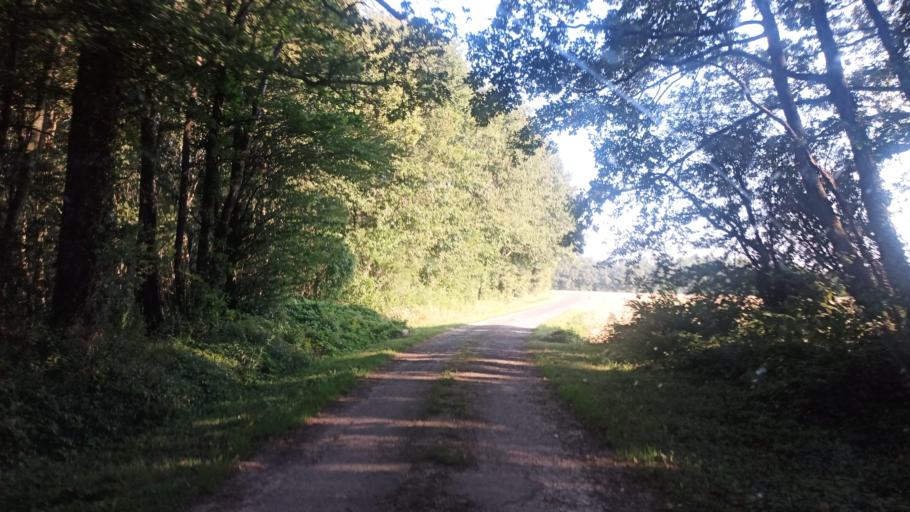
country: FR
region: Bourgogne
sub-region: Departement de l'Yonne
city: Saint-Valerien
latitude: 48.2268
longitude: 3.0803
